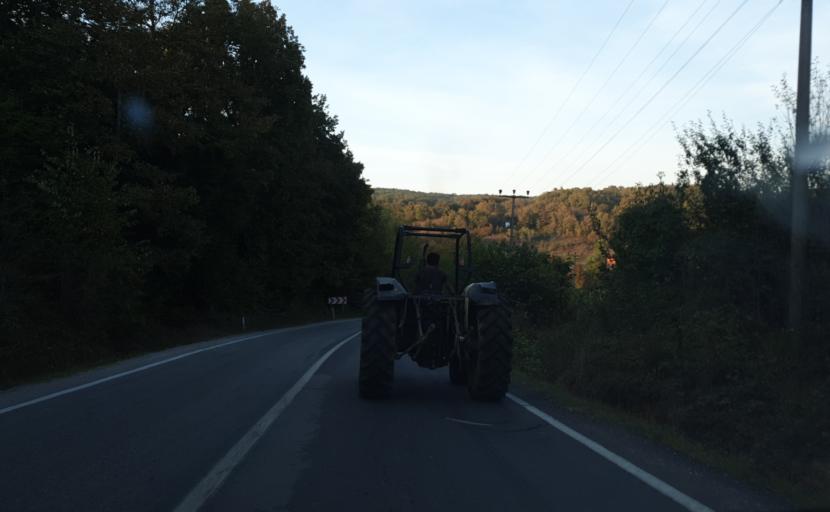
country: TR
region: Kirklareli
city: Sergen
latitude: 41.8326
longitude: 27.7887
